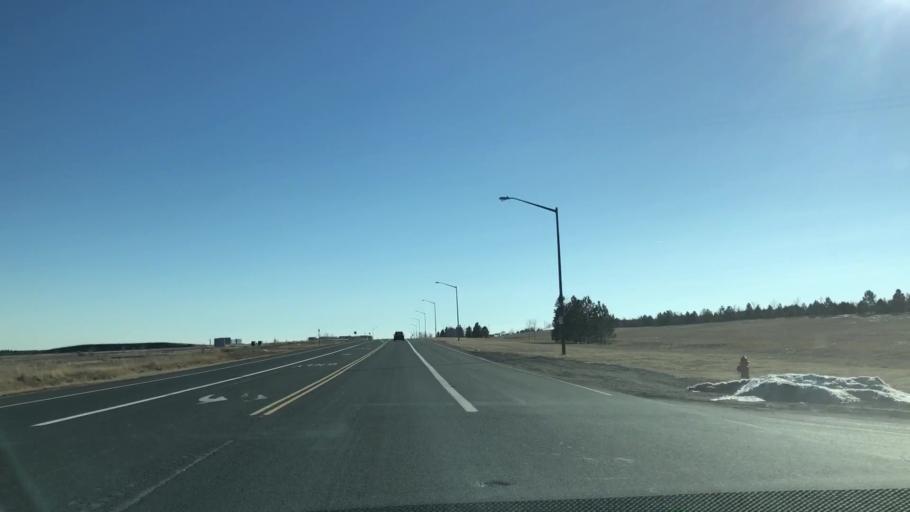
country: US
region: Colorado
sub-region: Weld County
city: Windsor
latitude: 40.4480
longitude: -104.9824
